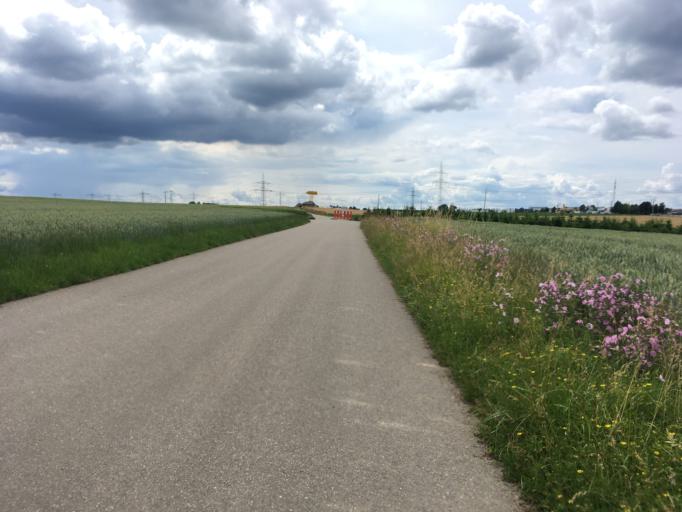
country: DE
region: Baden-Wuerttemberg
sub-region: Regierungsbezirk Stuttgart
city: Bietigheim-Bissingen
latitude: 48.9546
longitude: 9.0949
